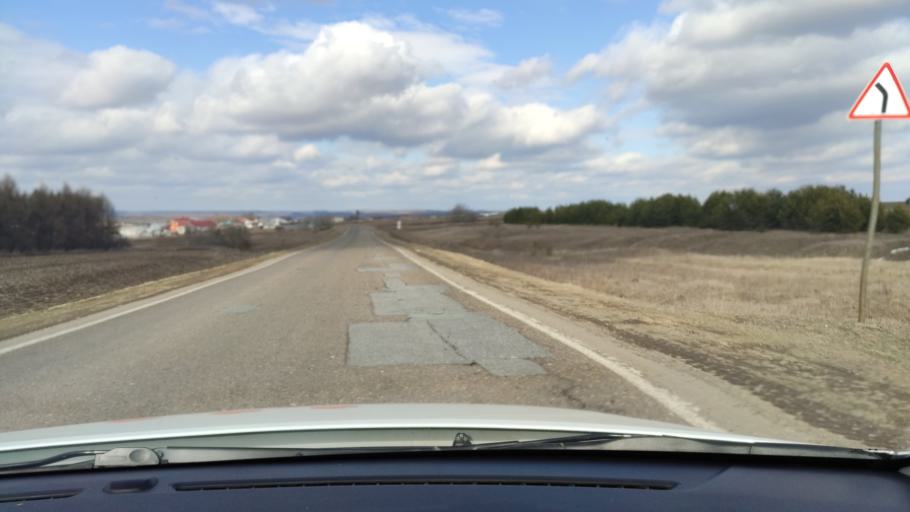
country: RU
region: Tatarstan
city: Vysokaya Gora
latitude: 56.1707
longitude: 49.2141
